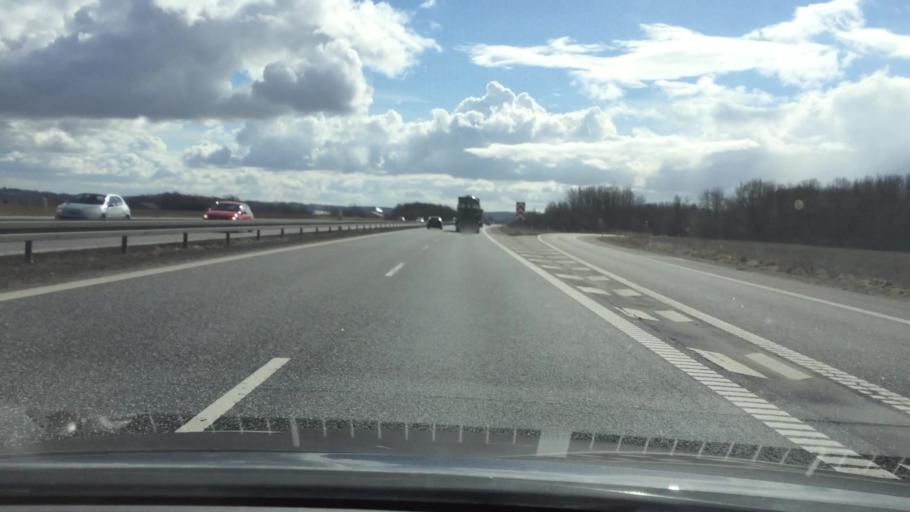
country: DK
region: Central Jutland
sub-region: Randers Kommune
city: Randers
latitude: 56.4956
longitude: 9.9792
